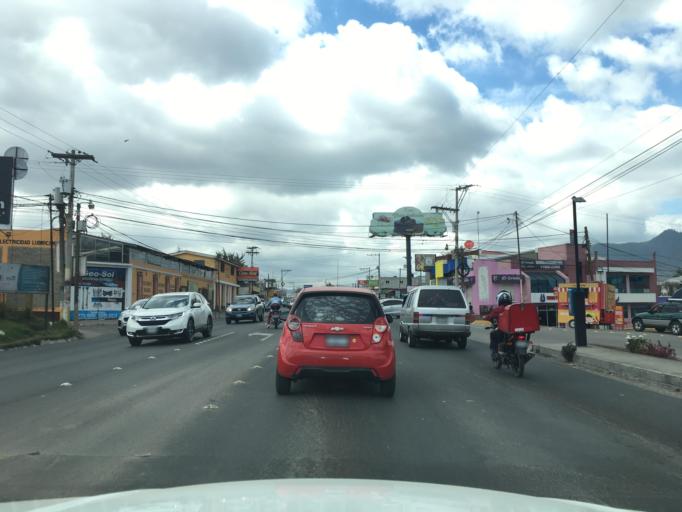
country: GT
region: Quetzaltenango
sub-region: Municipio de La Esperanza
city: La Esperanza
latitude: 14.8649
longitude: -91.5586
